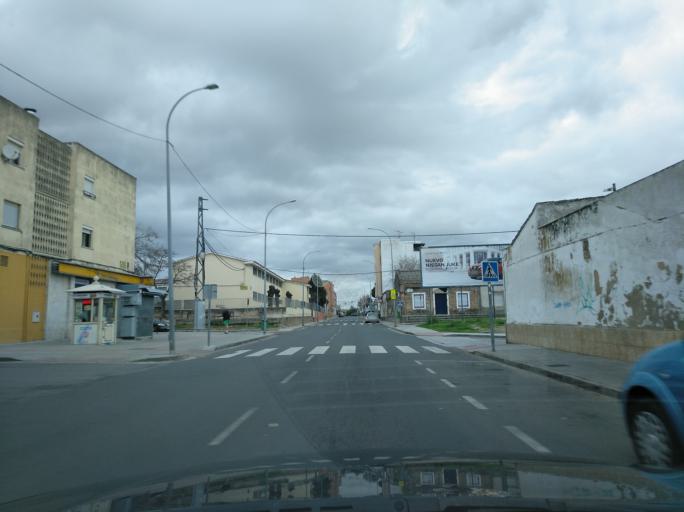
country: ES
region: Extremadura
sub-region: Provincia de Badajoz
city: Badajoz
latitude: 38.8923
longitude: -6.9800
